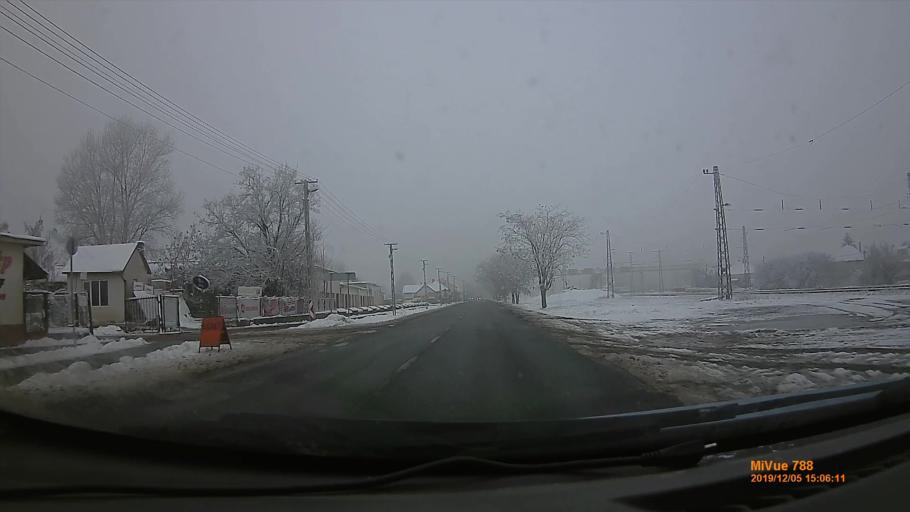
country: HU
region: Szabolcs-Szatmar-Bereg
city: Rakamaz
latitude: 48.1166
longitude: 21.4794
